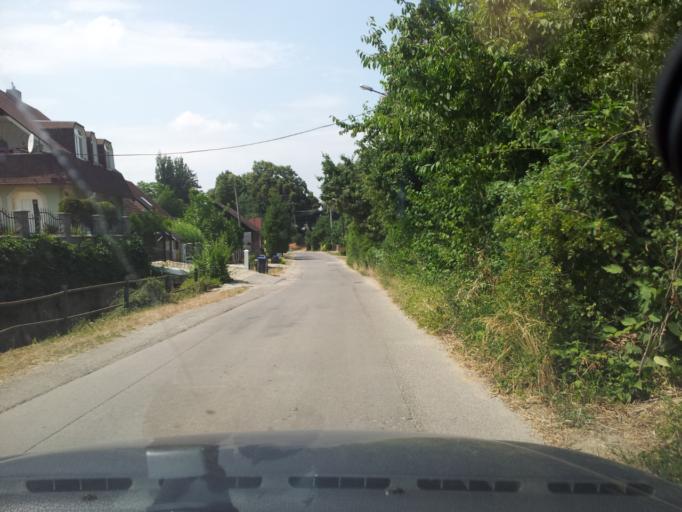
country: SK
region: Trenciansky
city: Nova Dubnica
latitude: 48.9105
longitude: 18.1015
